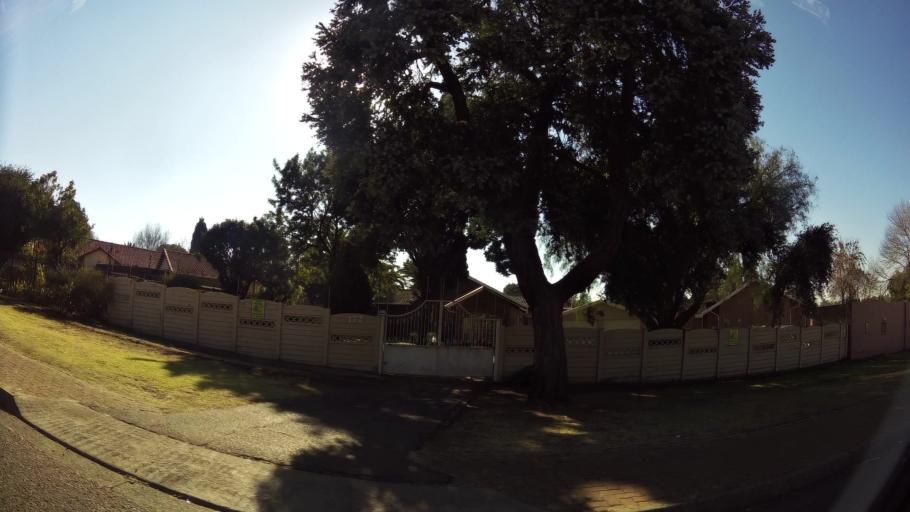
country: ZA
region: Gauteng
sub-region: Ekurhuleni Metropolitan Municipality
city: Germiston
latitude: -26.3357
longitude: 28.1029
